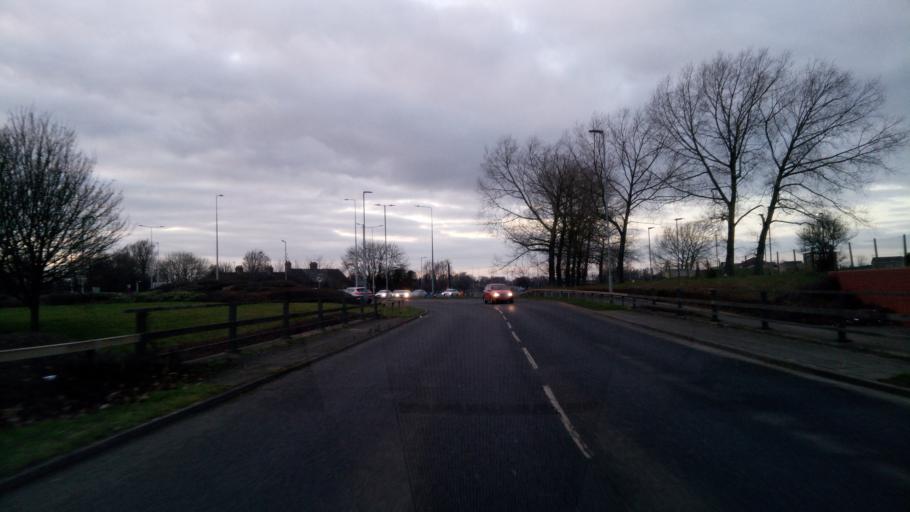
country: GB
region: England
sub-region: Peterborough
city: Peterborough
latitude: 52.5520
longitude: -0.2257
